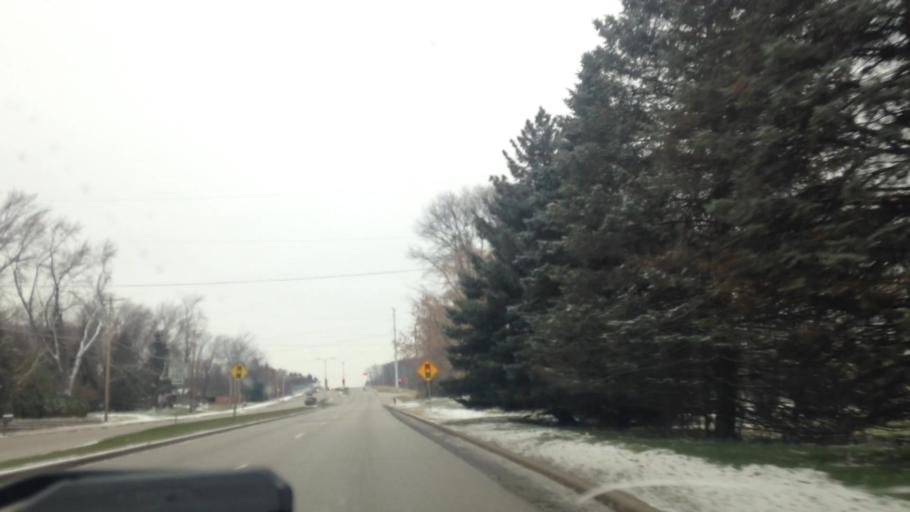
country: US
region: Wisconsin
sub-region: Waukesha County
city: Butler
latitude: 43.1218
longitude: -88.1051
